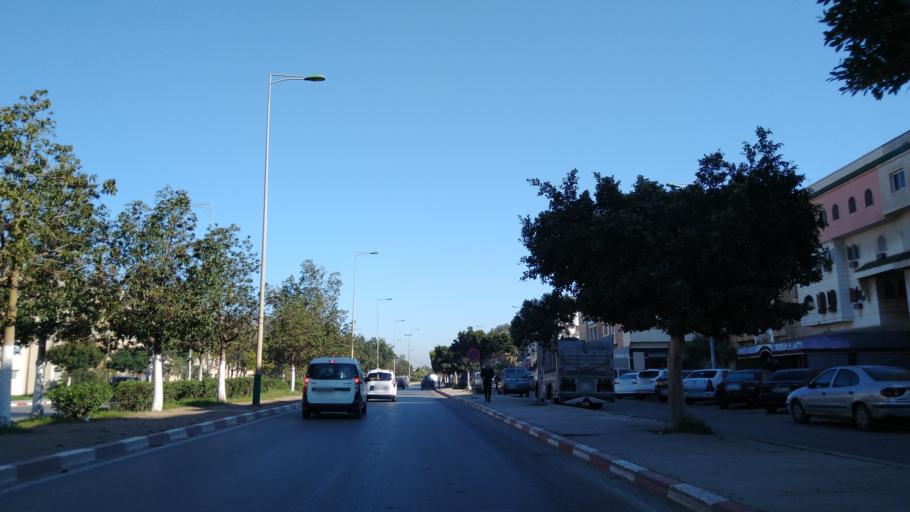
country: MA
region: Rabat-Sale-Zemmour-Zaer
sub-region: Skhirate-Temara
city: Temara
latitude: 33.9286
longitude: -6.8917
